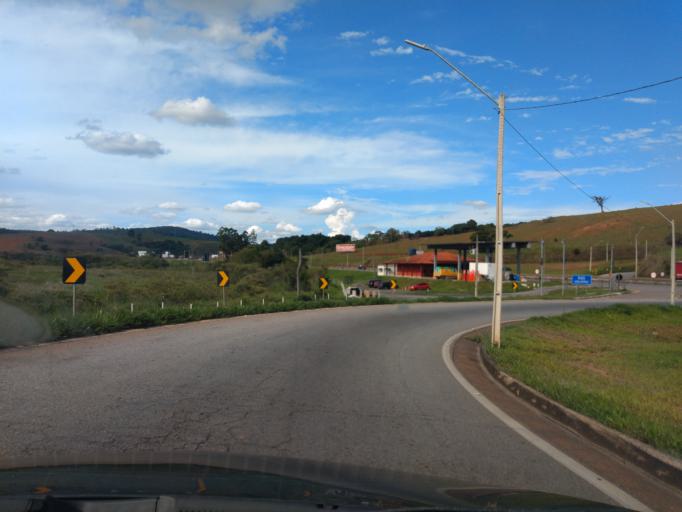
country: BR
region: Minas Gerais
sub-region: Tres Coracoes
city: Tres Coracoes
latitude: -21.6556
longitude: -45.3026
